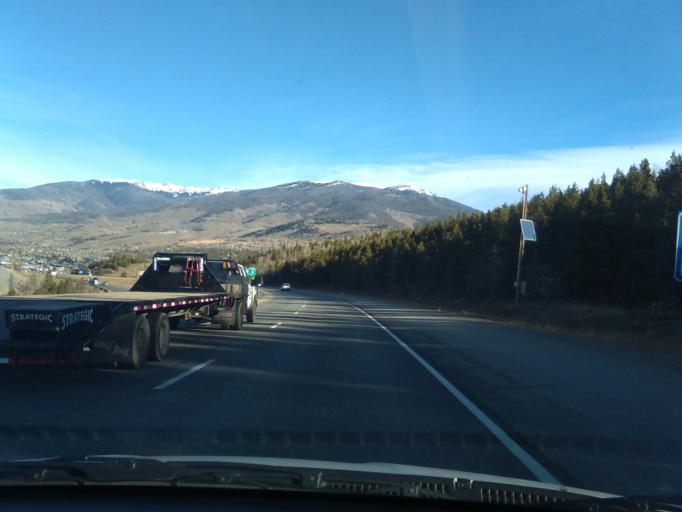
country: US
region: Colorado
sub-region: Summit County
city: Silverthorne
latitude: 39.6137
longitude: -106.0733
